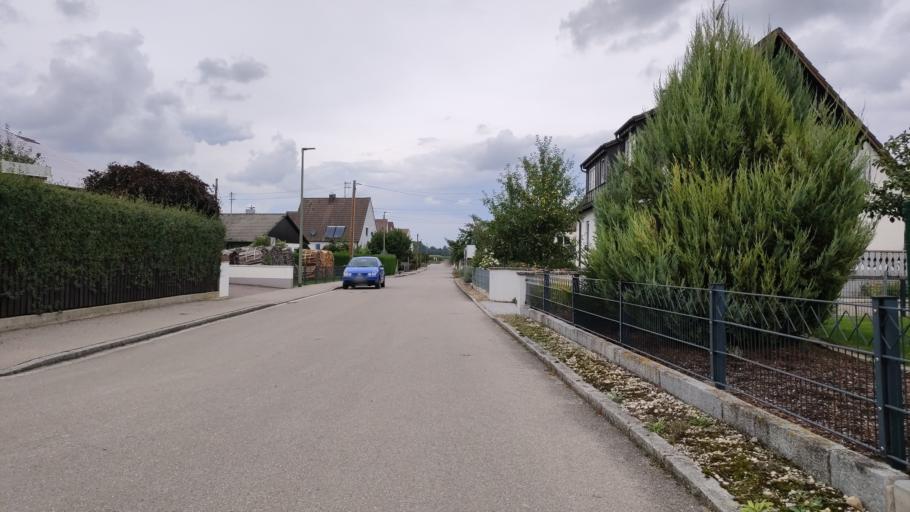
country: DE
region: Bavaria
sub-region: Swabia
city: Wehringen
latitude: 48.2499
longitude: 10.7984
